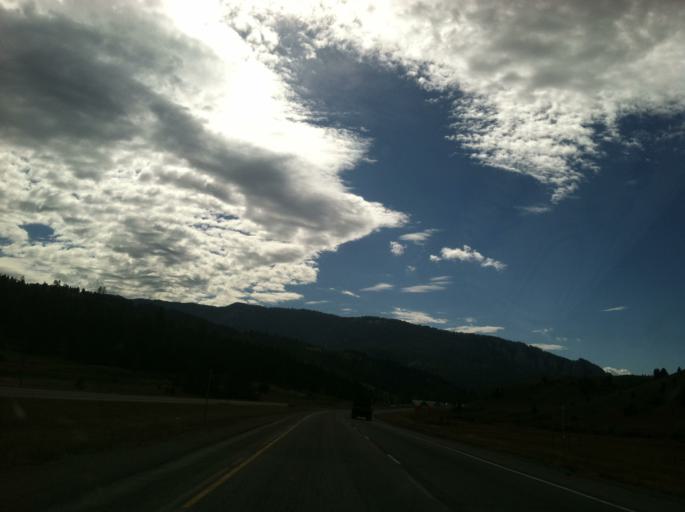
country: US
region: Montana
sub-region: Gallatin County
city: Bozeman
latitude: 45.6549
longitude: -110.8509
